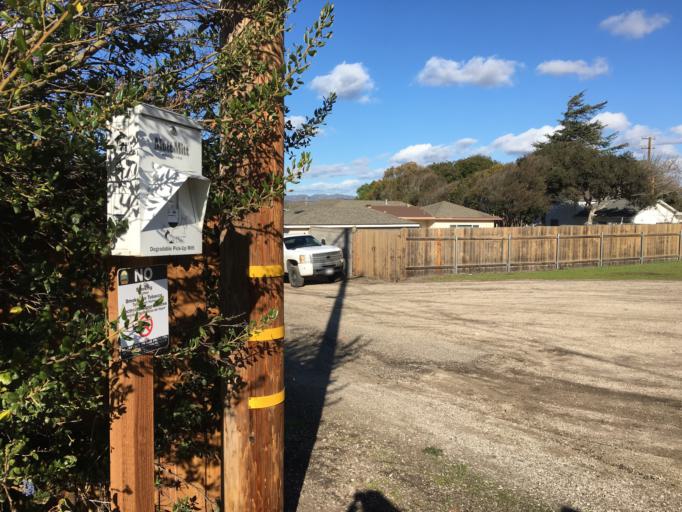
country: US
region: California
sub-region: Santa Barbara County
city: Lompoc
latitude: 34.6319
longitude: -120.4549
